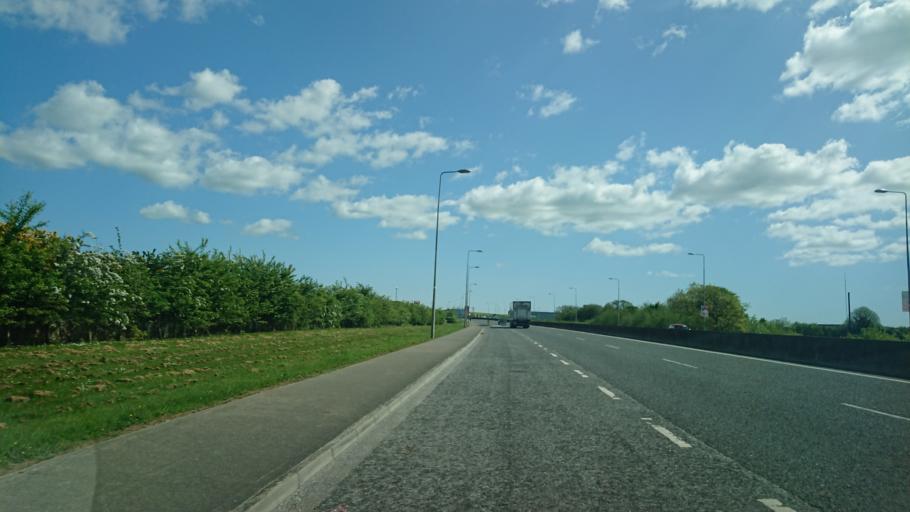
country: IE
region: Munster
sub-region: Waterford
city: Waterford
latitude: 52.2460
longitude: -7.1718
